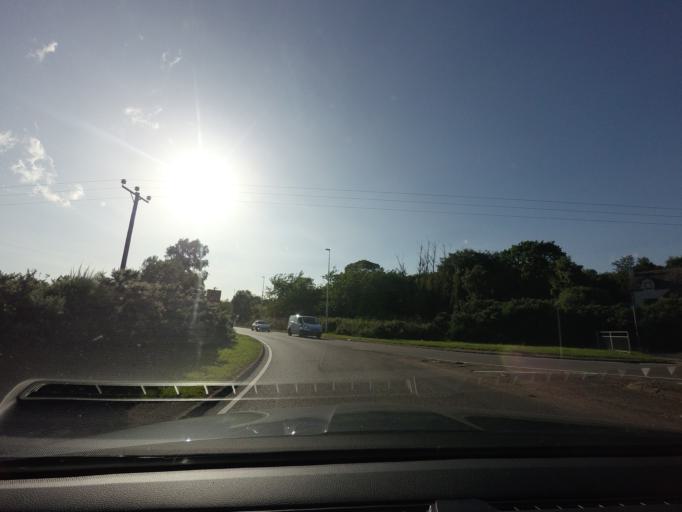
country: GB
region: Scotland
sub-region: Highland
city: Conon Bridge
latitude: 57.5405
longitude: -4.3372
